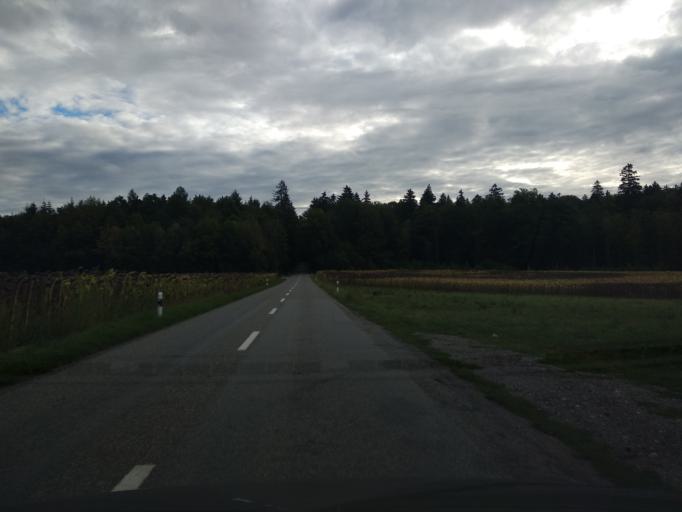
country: DE
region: Baden-Wuerttemberg
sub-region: Freiburg Region
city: Busingen
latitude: 47.6693
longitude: 8.7117
